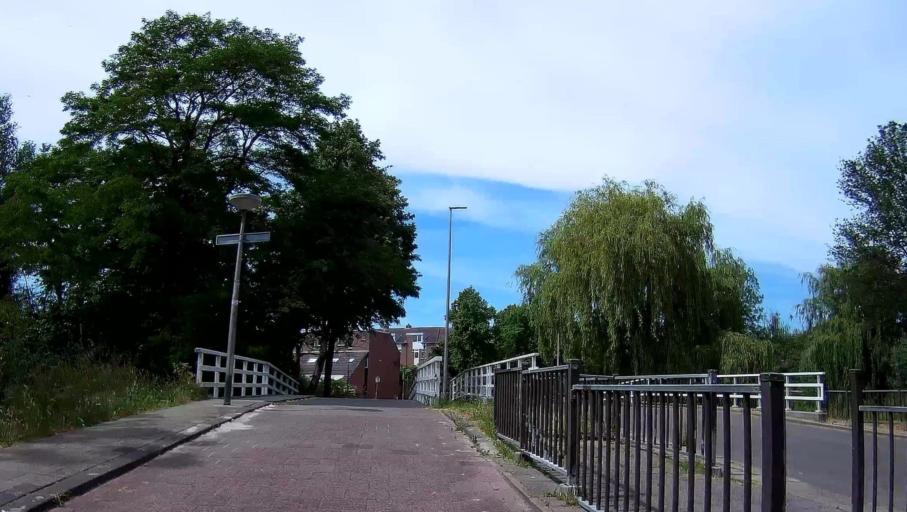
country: NL
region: South Holland
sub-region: Gemeente Delft
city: Delft
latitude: 51.9864
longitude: 4.3610
